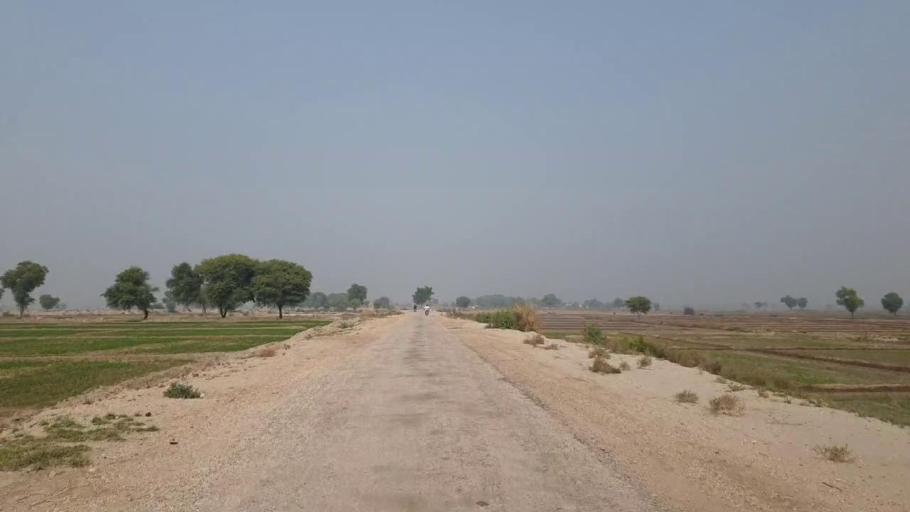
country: PK
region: Sindh
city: Bhan
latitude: 26.5167
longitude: 67.6897
